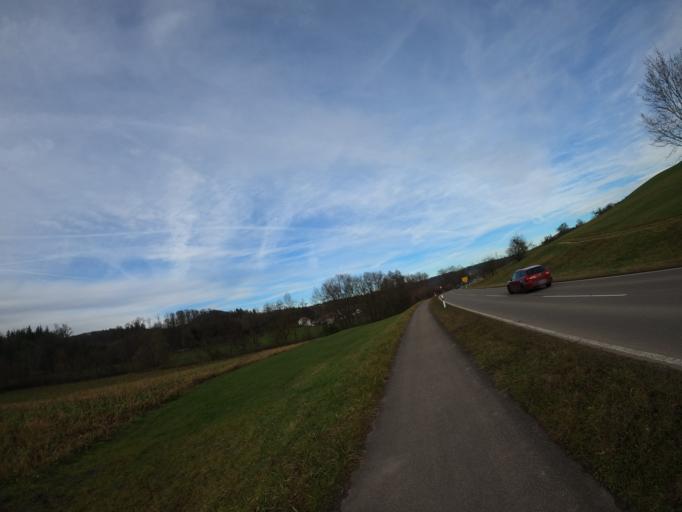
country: DE
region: Baden-Wuerttemberg
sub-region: Regierungsbezirk Stuttgart
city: Ottenbach
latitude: 48.7181
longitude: 9.7359
